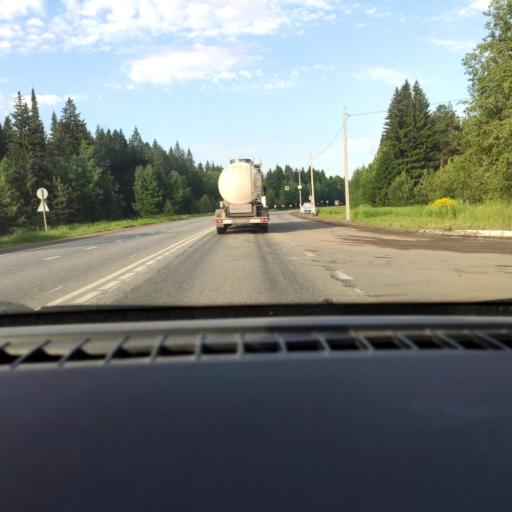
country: RU
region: Udmurtiya
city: Votkinsk
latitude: 57.0164
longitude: 53.9006
